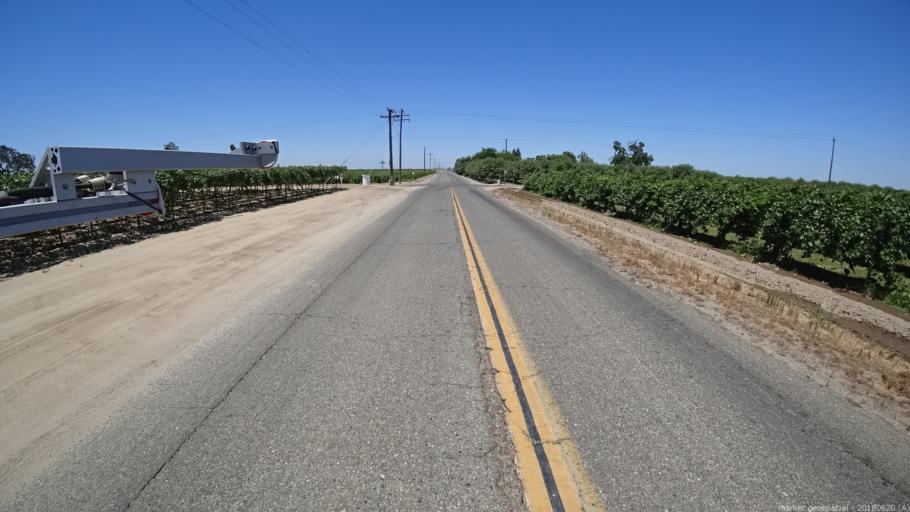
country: US
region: California
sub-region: Madera County
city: Parkwood
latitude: 36.8658
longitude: -120.0368
